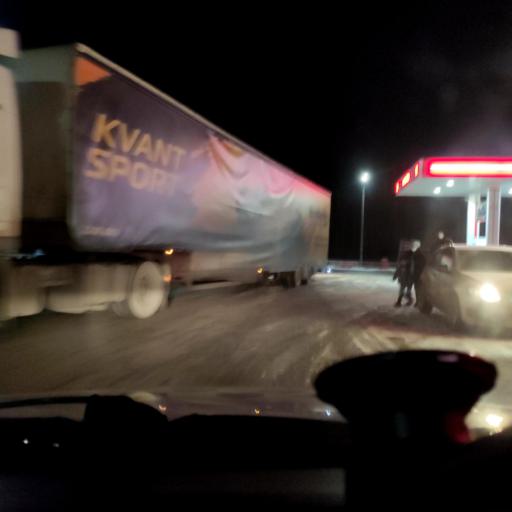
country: RU
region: Perm
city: Kungur
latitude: 57.3272
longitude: 56.9562
